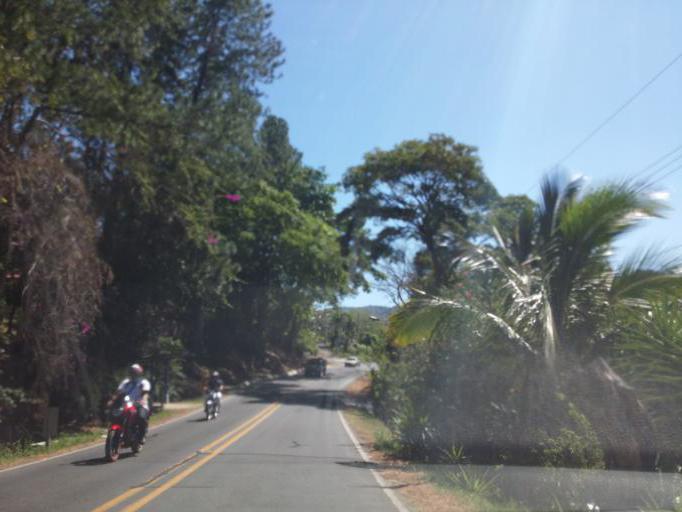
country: CR
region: Heredia
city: Colon
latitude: 9.8984
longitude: -84.2352
